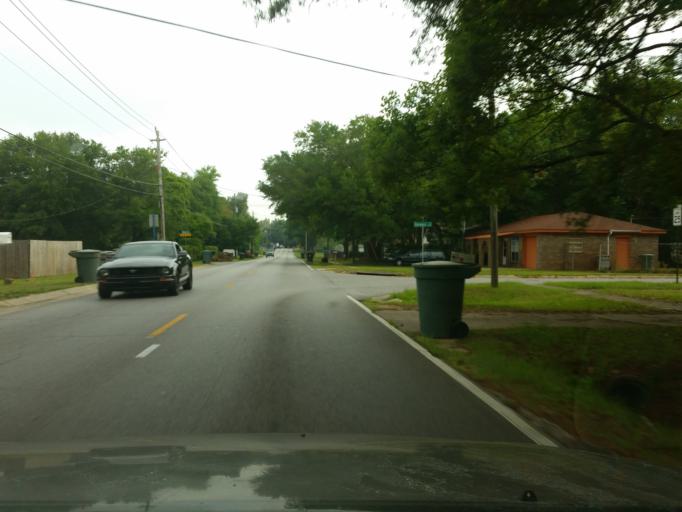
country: US
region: Florida
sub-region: Escambia County
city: Bellview
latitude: 30.4452
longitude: -87.3110
